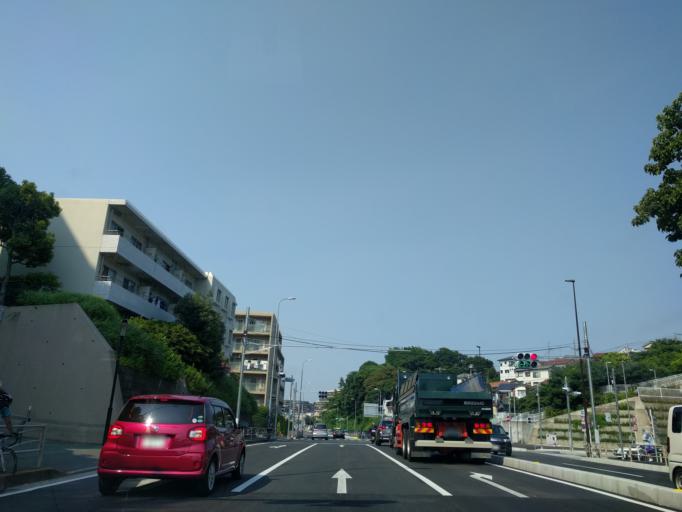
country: JP
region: Kanagawa
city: Yokohama
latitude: 35.4944
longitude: 139.6582
